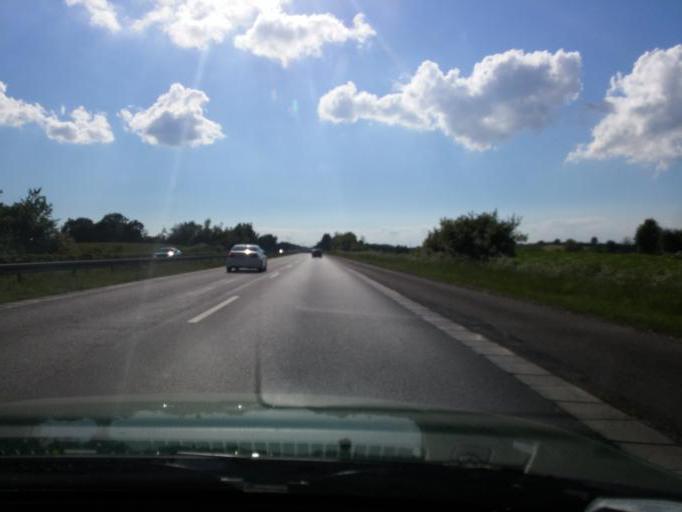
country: DK
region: South Denmark
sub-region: Assens Kommune
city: Vissenbjerg
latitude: 55.4110
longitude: 10.0867
